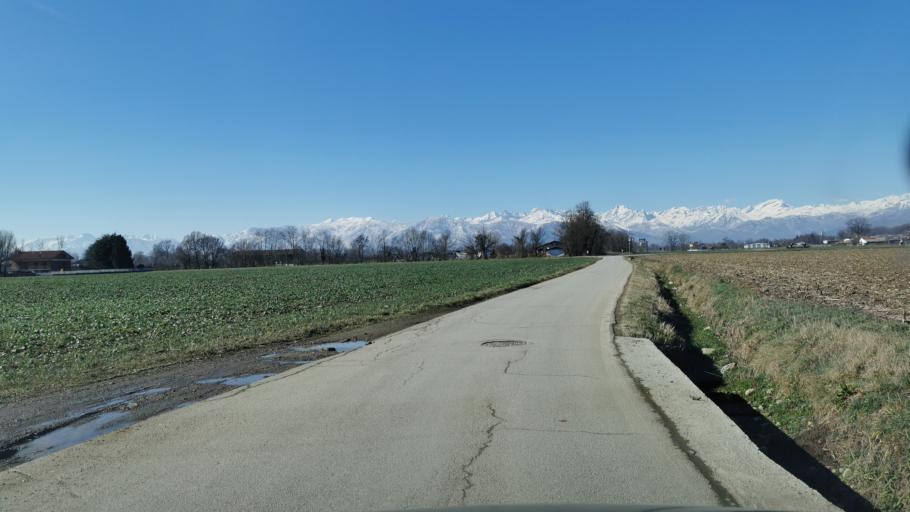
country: IT
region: Piedmont
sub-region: Provincia di Torino
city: Leini
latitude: 45.2115
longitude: 7.6900
